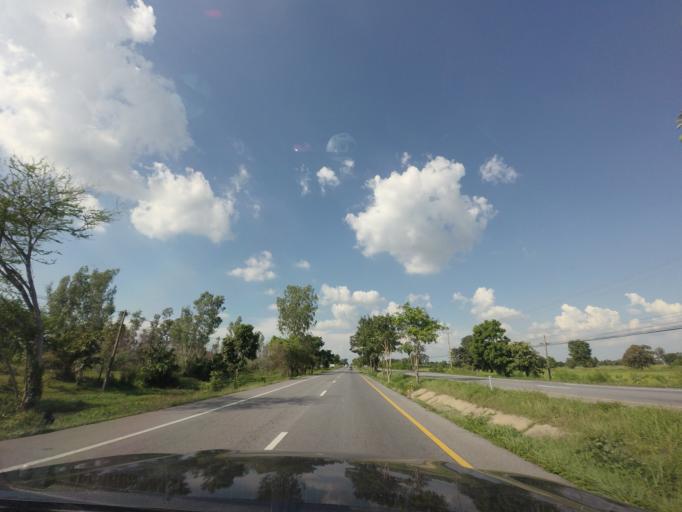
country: TH
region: Khon Kaen
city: Phon
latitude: 15.7179
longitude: 102.5905
